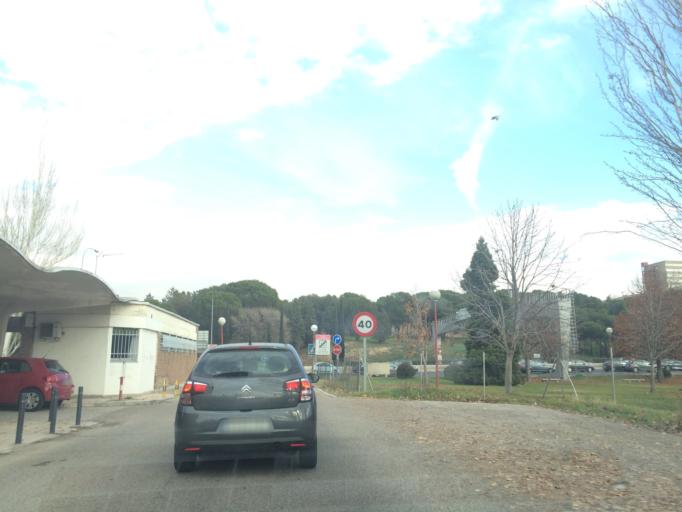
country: ES
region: Madrid
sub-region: Provincia de Madrid
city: Moncloa-Aravaca
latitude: 40.4468
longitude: -3.7357
